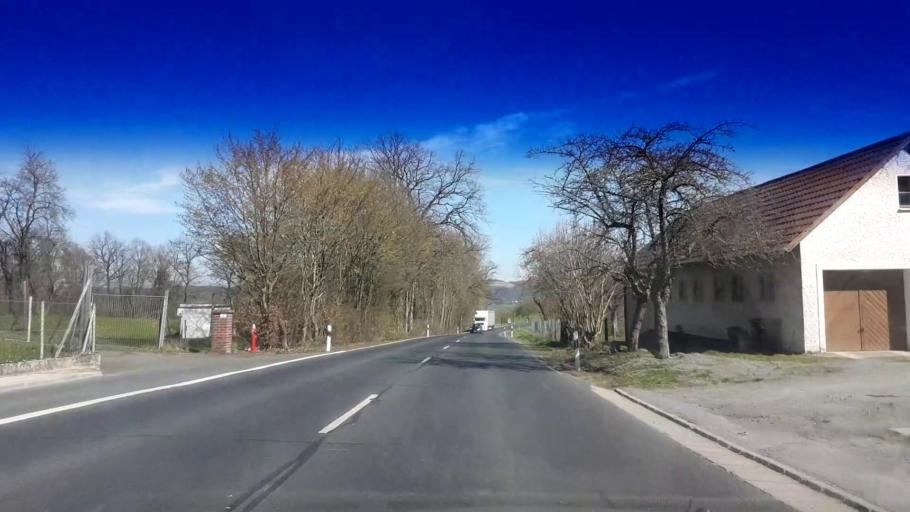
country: DE
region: Bavaria
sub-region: Upper Franconia
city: Bindlach
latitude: 50.0102
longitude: 11.6289
